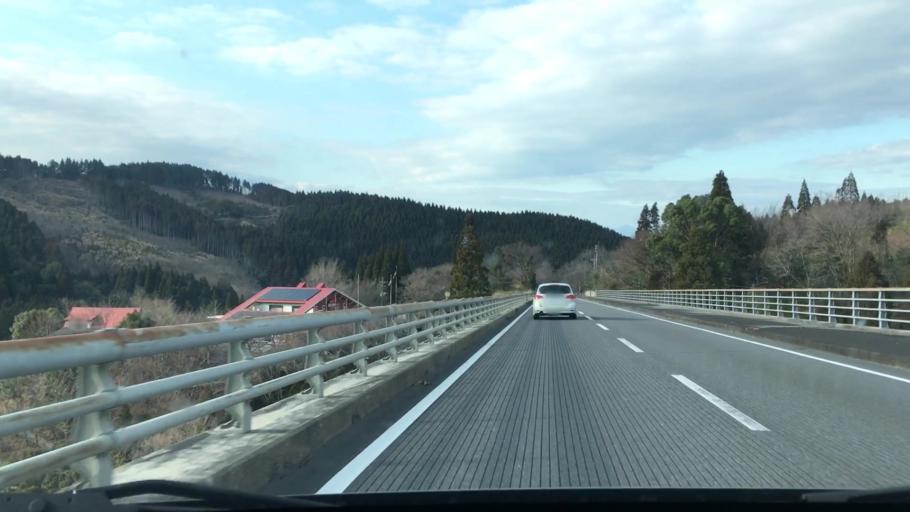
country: JP
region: Miyazaki
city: Miyazaki-shi
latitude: 31.7996
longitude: 131.3035
